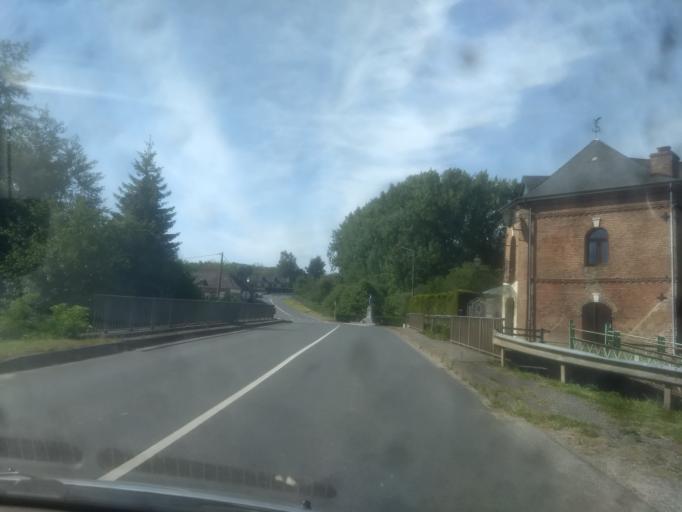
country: FR
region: Picardie
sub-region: Departement de la Somme
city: Doullens
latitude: 50.1640
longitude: 2.3003
